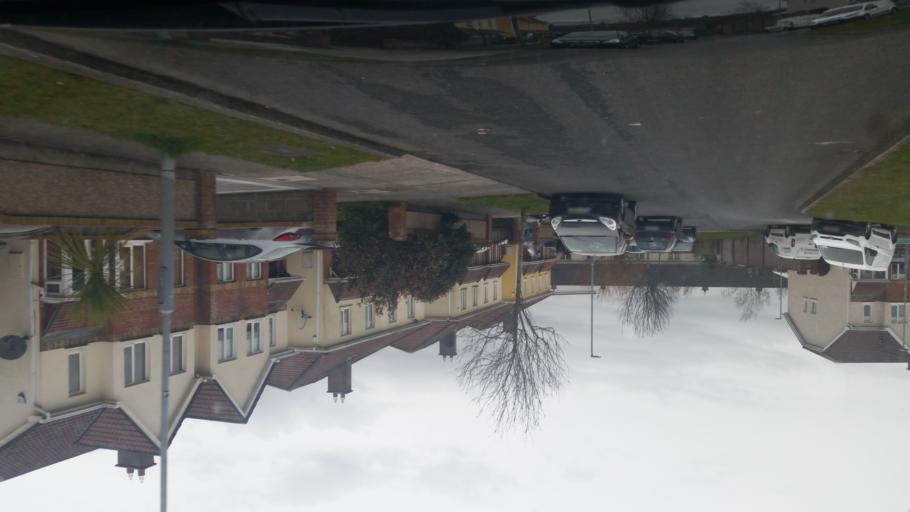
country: IE
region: Leinster
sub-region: Fingal County
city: Blanchardstown
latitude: 53.4024
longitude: -6.3866
